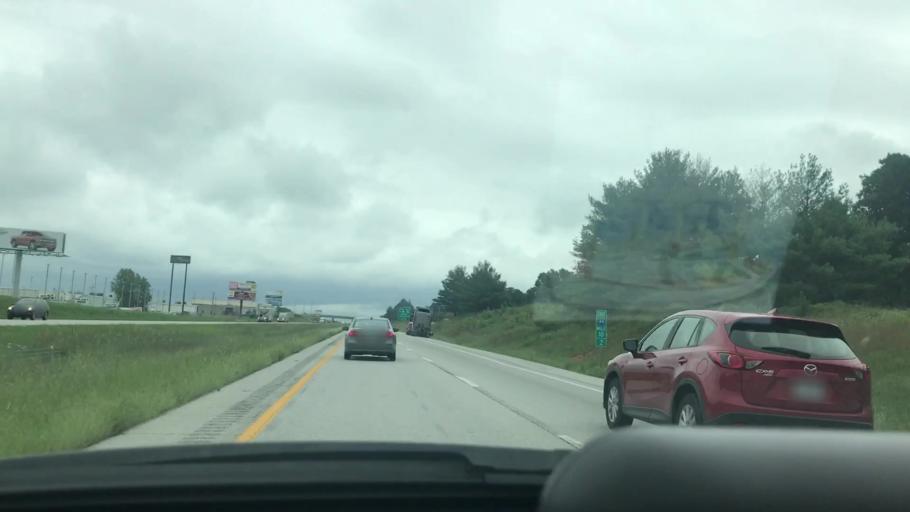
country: US
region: Missouri
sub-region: Jasper County
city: Duquesne
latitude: 37.0519
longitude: -94.4551
